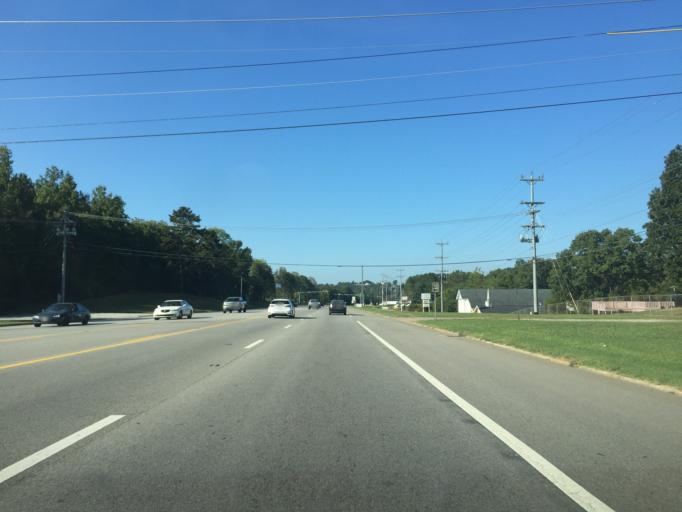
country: US
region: Tennessee
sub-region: Hamilton County
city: Harrison
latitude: 35.1098
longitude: -85.1418
